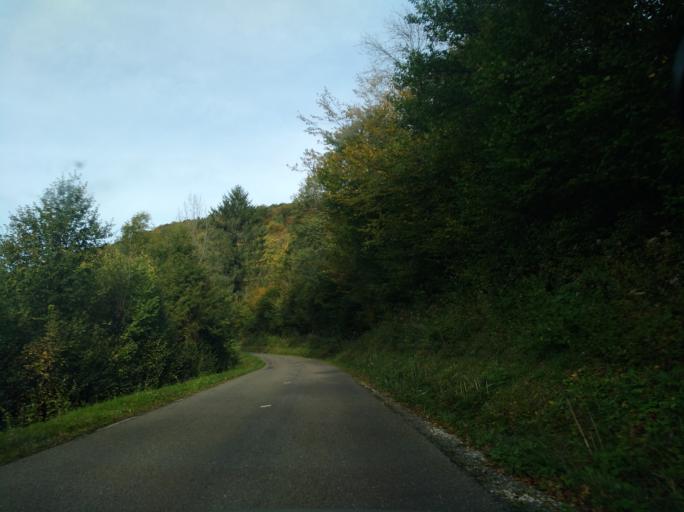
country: FR
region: Bourgogne
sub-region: Departement de Saone-et-Loire
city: Cuiseaux
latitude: 46.4811
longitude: 5.4785
